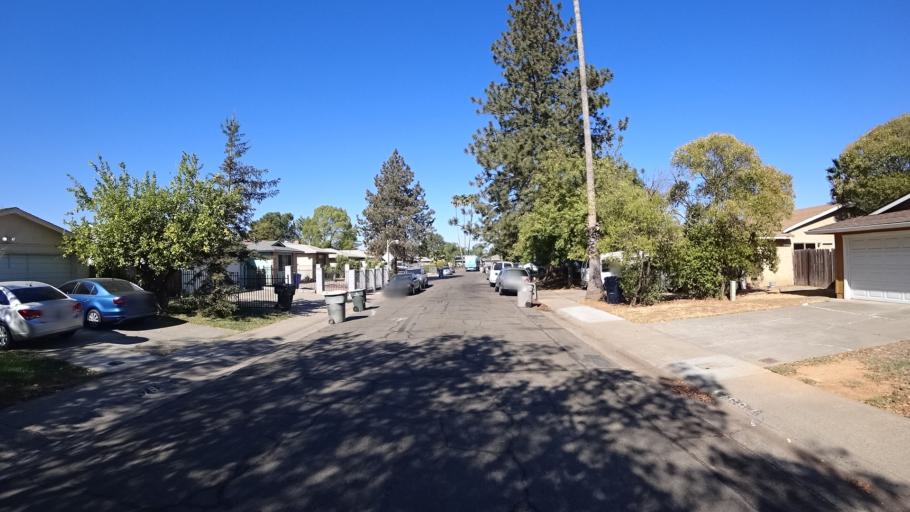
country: US
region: California
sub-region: Sacramento County
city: Parkway
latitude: 38.4783
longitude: -121.4364
